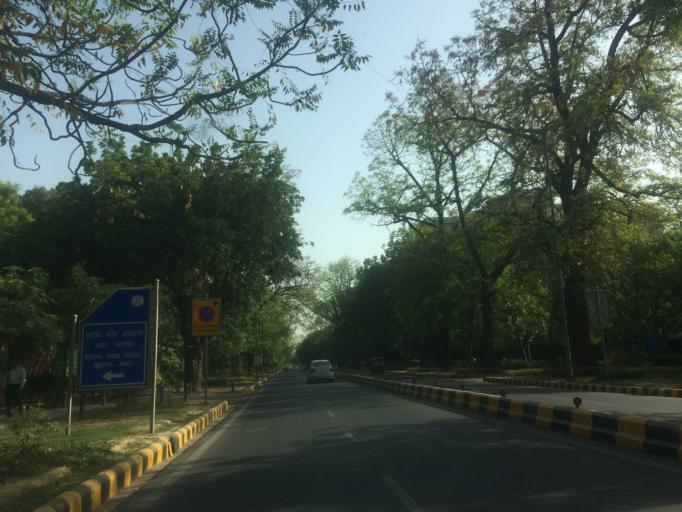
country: IN
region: NCT
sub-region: New Delhi
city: New Delhi
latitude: 28.6181
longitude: 77.2314
